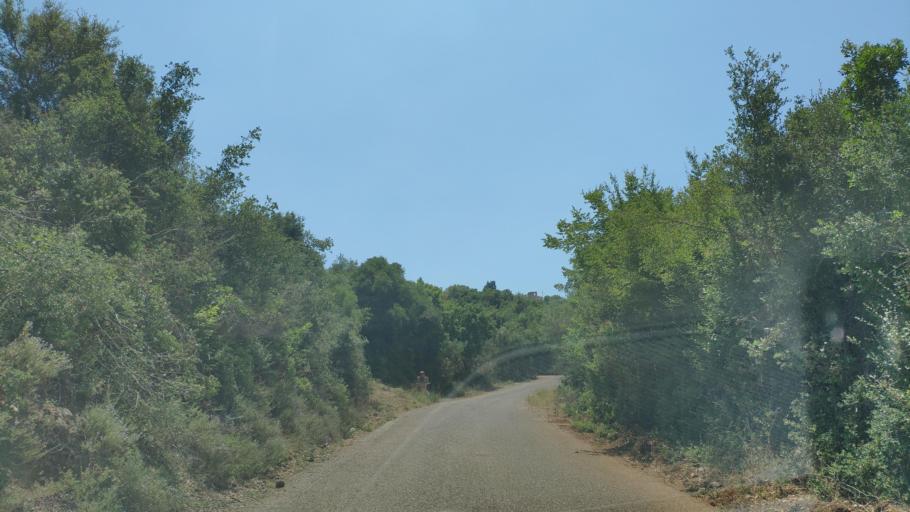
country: GR
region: West Greece
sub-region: Nomos Aitolias kai Akarnanias
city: Fitiai
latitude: 38.7156
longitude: 21.1763
